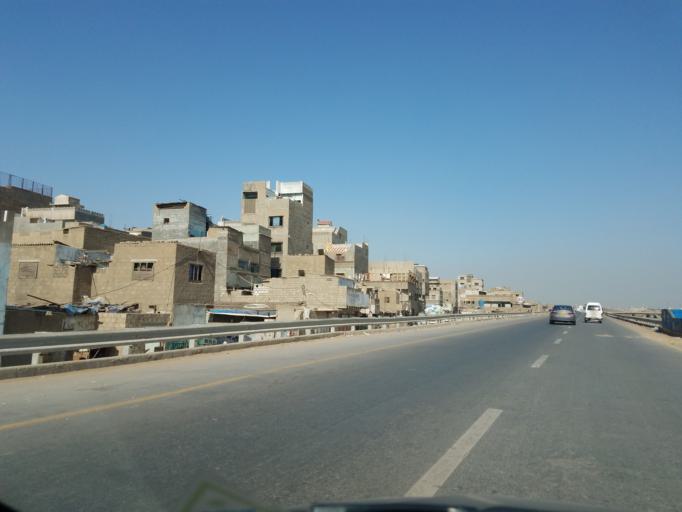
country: PK
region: Sindh
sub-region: Karachi District
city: Karachi
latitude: 24.8787
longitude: 66.9880
